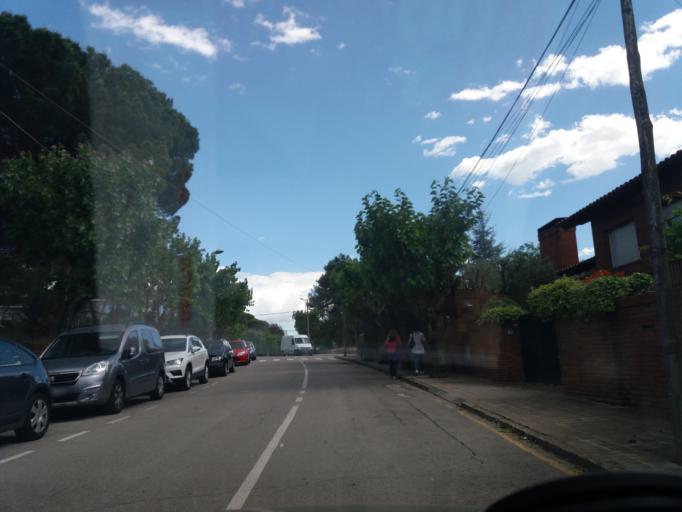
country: ES
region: Catalonia
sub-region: Provincia de Barcelona
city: Santpedor
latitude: 41.7570
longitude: 1.8388
